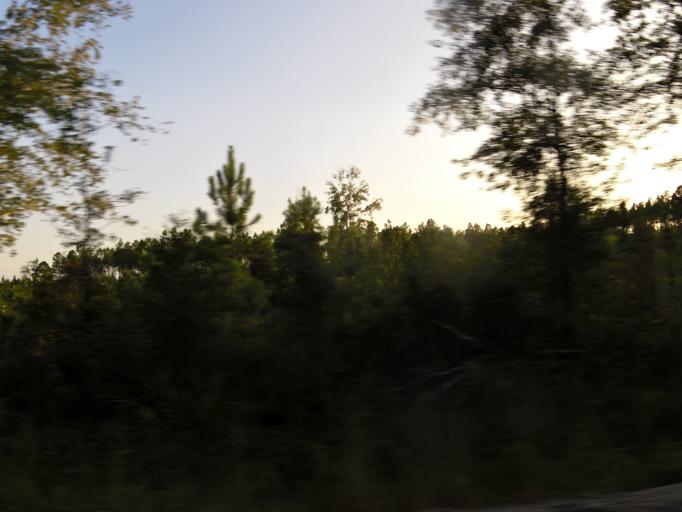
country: US
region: Florida
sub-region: Duval County
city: Baldwin
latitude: 30.3884
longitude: -82.0517
